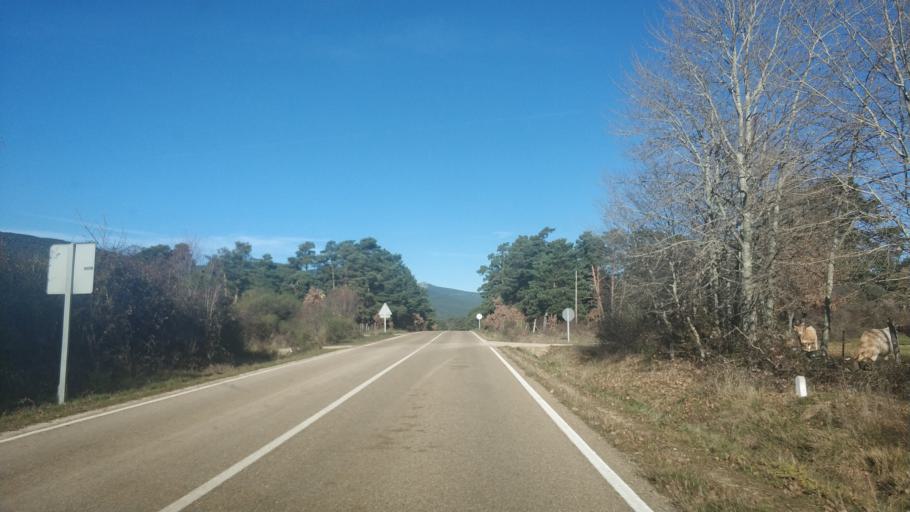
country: ES
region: Castille and Leon
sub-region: Provincia de Soria
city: Vinuesa
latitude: 41.9169
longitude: -2.7554
